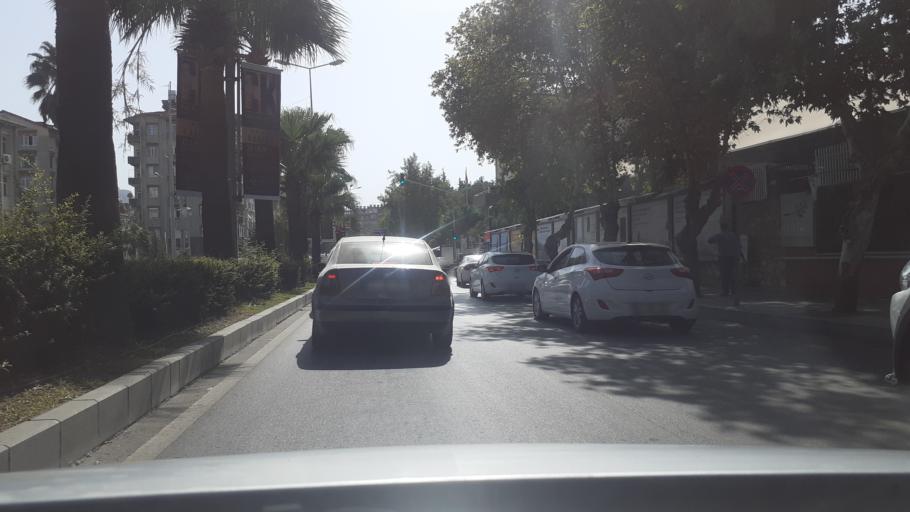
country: TR
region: Hatay
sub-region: Antakya Ilcesi
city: Antakya
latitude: 36.2116
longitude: 36.1598
